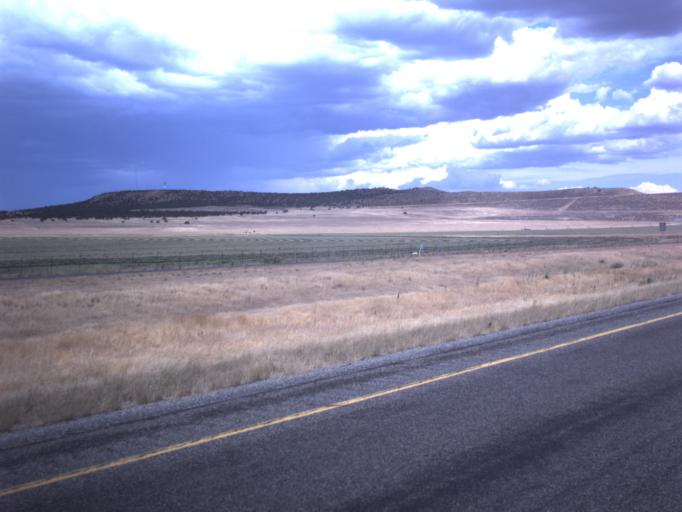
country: US
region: Idaho
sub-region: Oneida County
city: Malad City
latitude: 41.9714
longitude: -112.7769
